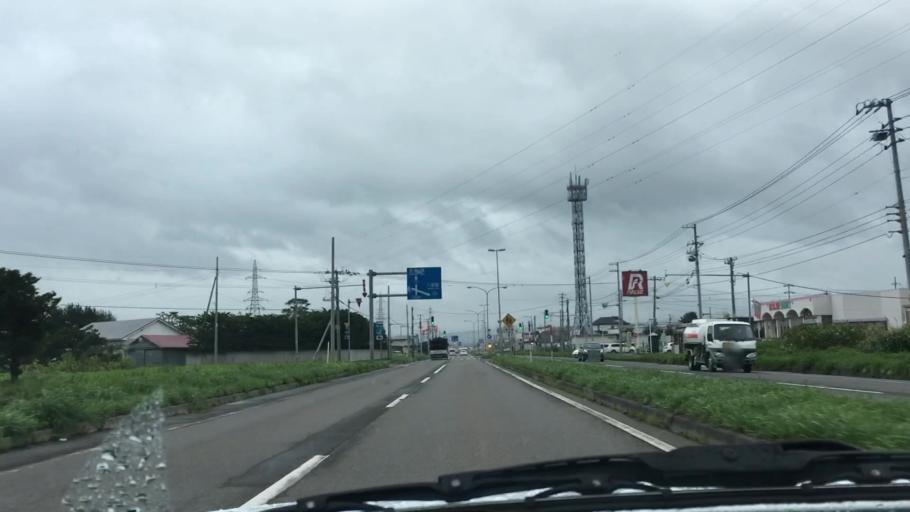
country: JP
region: Hokkaido
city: Nanae
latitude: 42.2595
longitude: 140.2770
